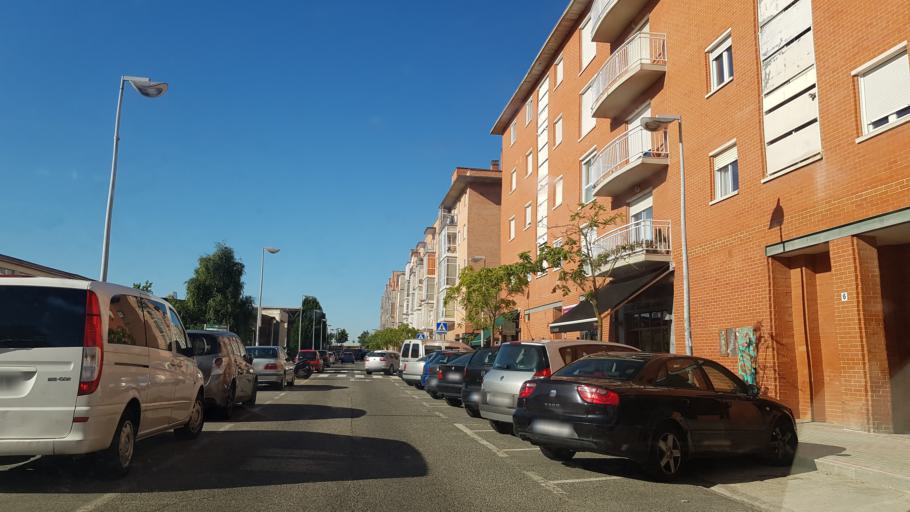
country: ES
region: Navarre
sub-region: Provincia de Navarra
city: Burlata
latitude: 42.8103
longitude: -1.6179
